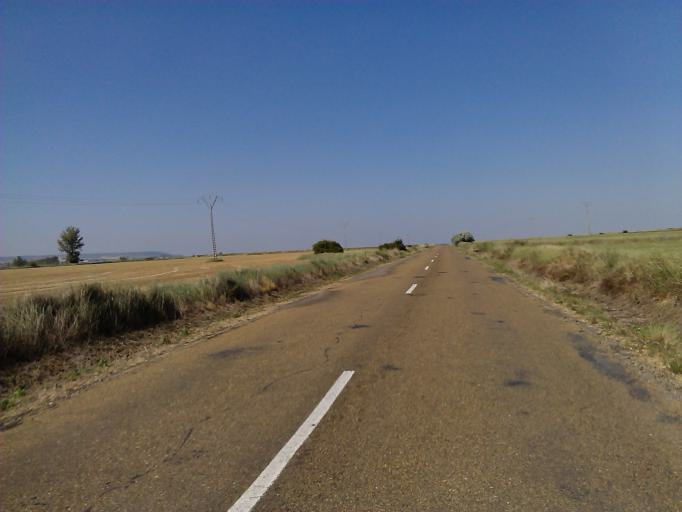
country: ES
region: Castille and Leon
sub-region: Provincia de Palencia
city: Boadilla del Camino
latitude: 42.2495
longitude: -4.3669
